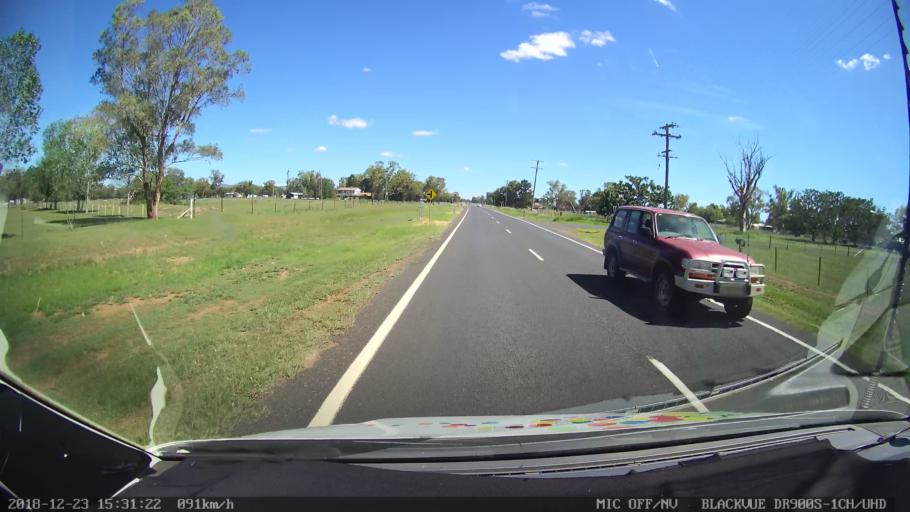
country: AU
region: New South Wales
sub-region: Tamworth Municipality
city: East Tamworth
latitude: -30.9711
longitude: 150.8671
